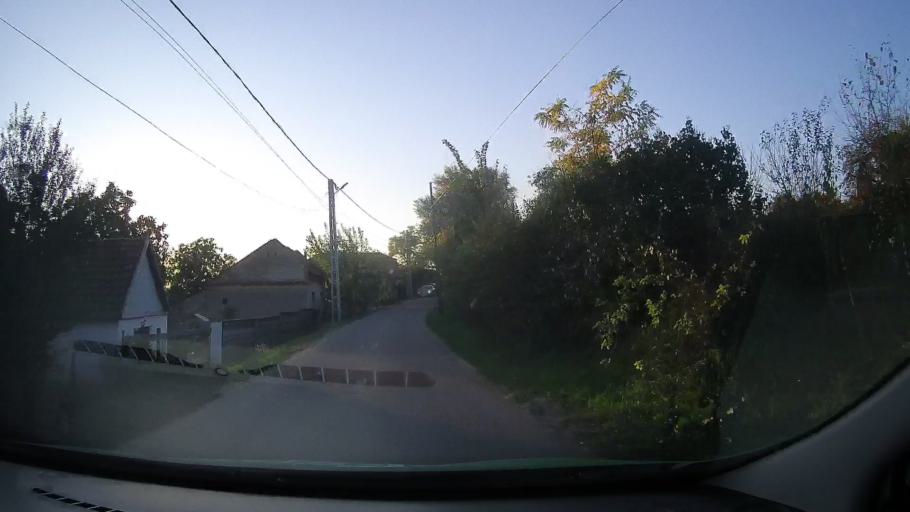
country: RO
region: Bihor
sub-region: Comuna Rosiori
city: Rosiori
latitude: 47.2500
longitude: 22.0007
